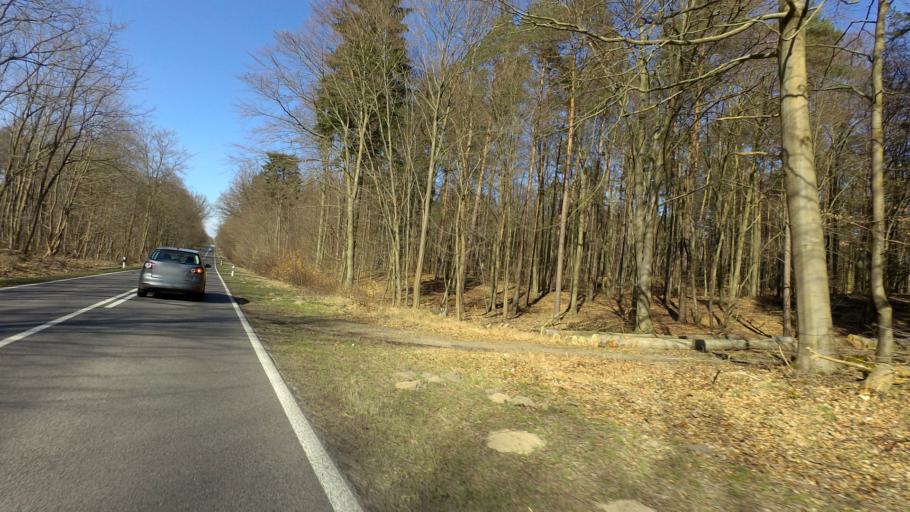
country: DE
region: Brandenburg
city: Eberswalde
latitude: 52.8093
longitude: 13.8344
